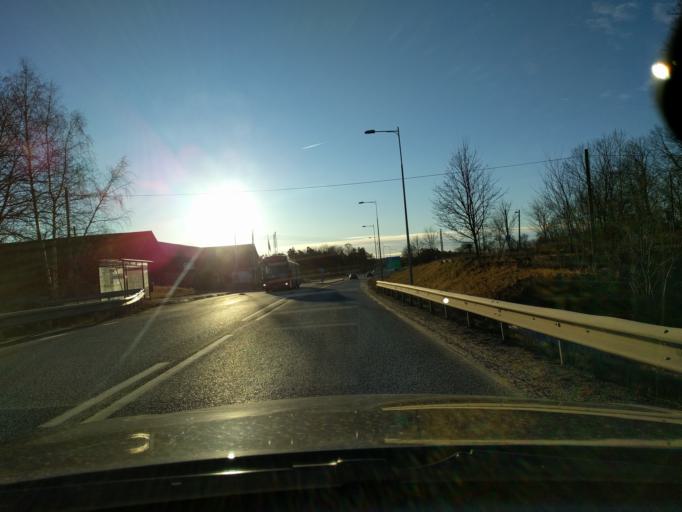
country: SE
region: Stockholm
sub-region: Taby Kommun
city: Taby
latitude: 59.4794
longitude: 18.0539
